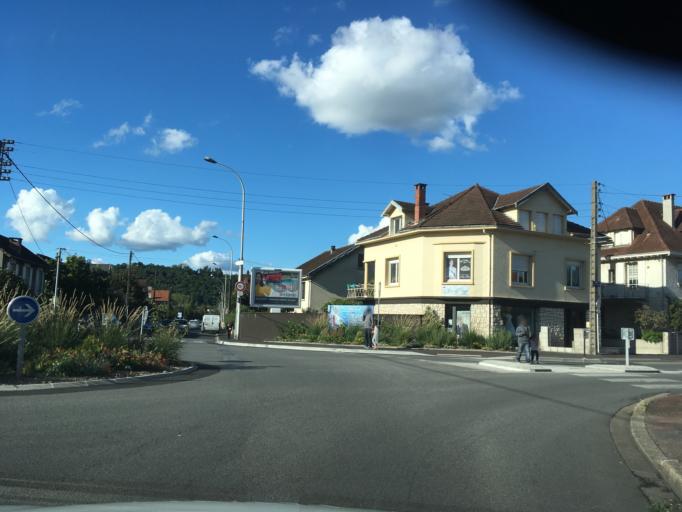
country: FR
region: Limousin
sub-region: Departement de la Correze
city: Brive-la-Gaillarde
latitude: 45.1564
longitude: 1.5042
